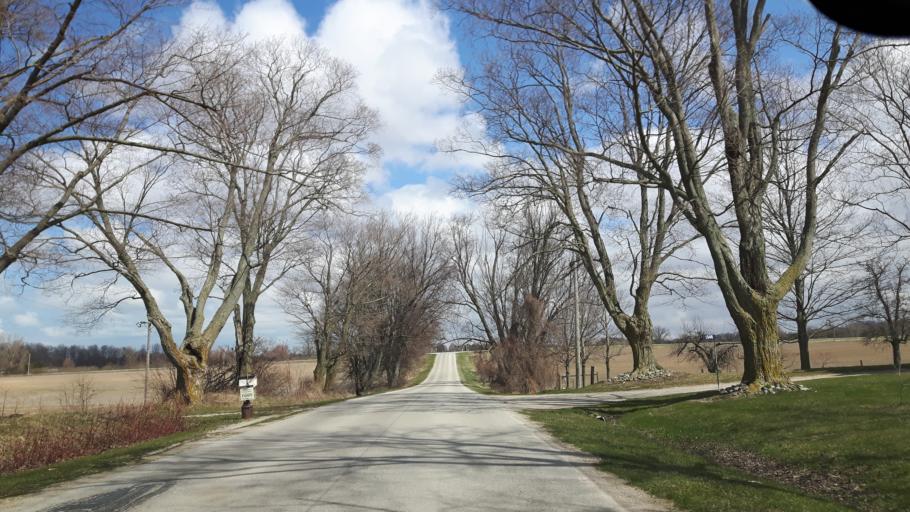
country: CA
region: Ontario
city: Goderich
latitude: 43.6400
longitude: -81.6846
